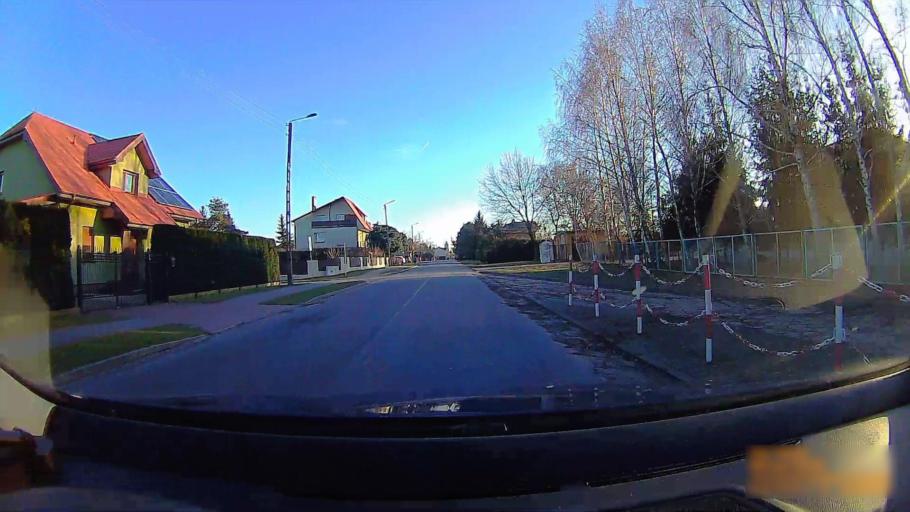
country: PL
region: Greater Poland Voivodeship
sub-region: Powiat koninski
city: Rychwal
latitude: 52.0740
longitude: 18.1662
